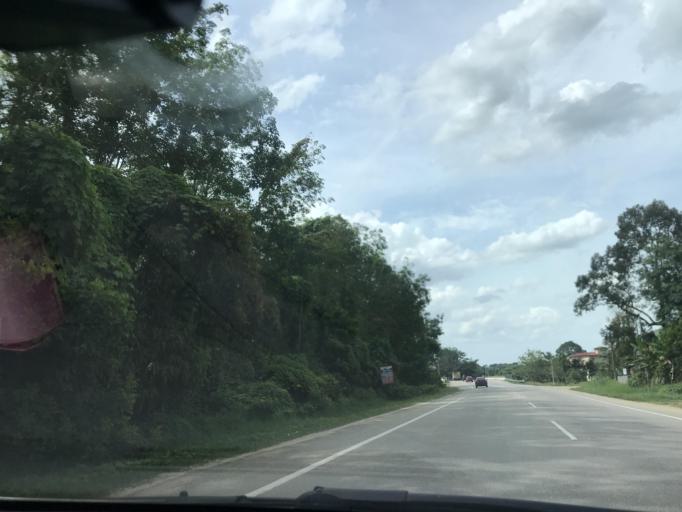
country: MY
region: Kelantan
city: Kampong Pangkal Kalong
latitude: 5.8962
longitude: 102.1843
